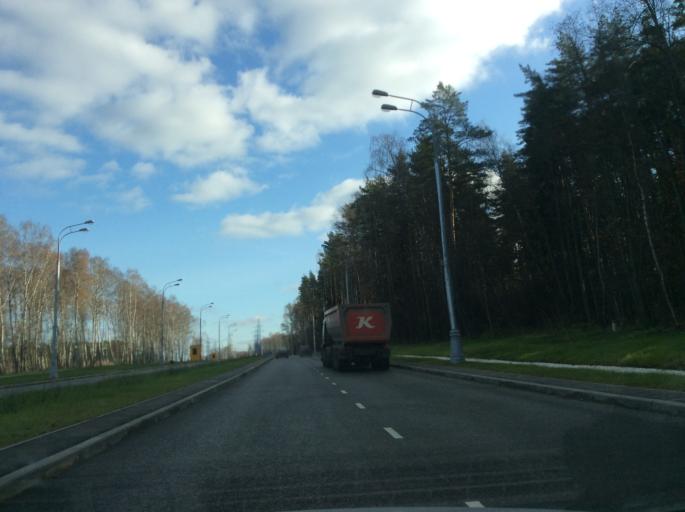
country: RU
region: Moskovskaya
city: Vatutinki
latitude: 55.4850
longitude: 37.3289
